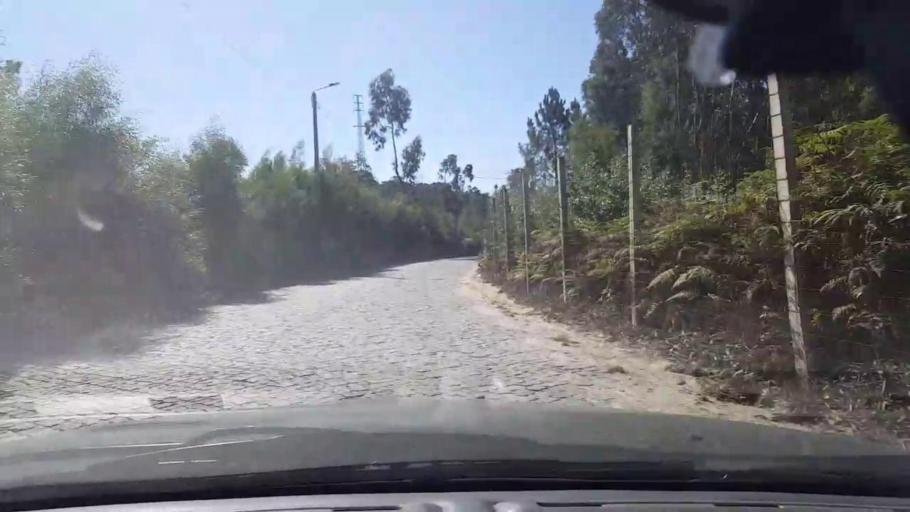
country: PT
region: Porto
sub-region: Maia
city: Gemunde
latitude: 41.2972
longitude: -8.6652
